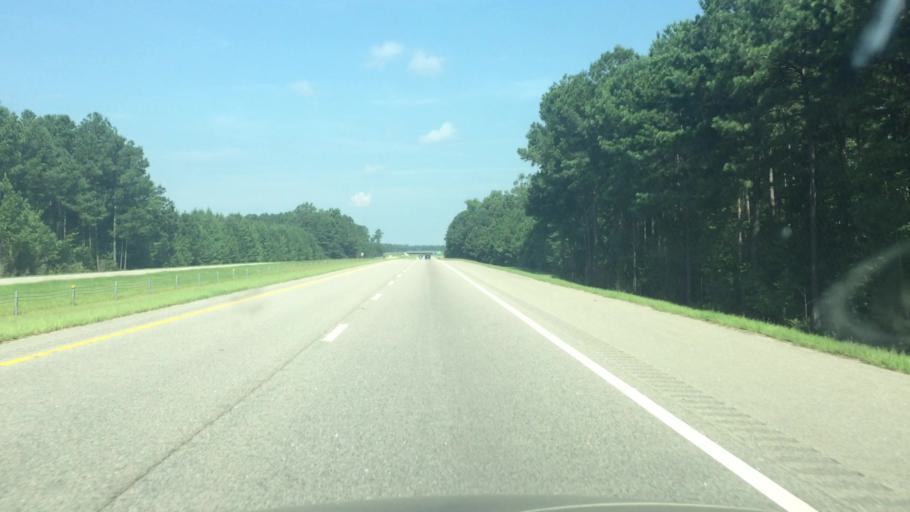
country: US
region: North Carolina
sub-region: Robeson County
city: Pembroke
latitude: 34.5961
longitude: -79.1853
